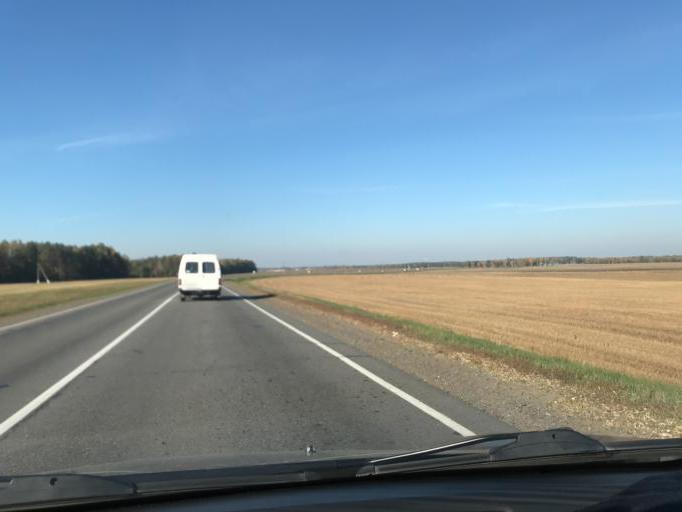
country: BY
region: Gomel
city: Parychy
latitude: 52.6589
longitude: 29.3622
